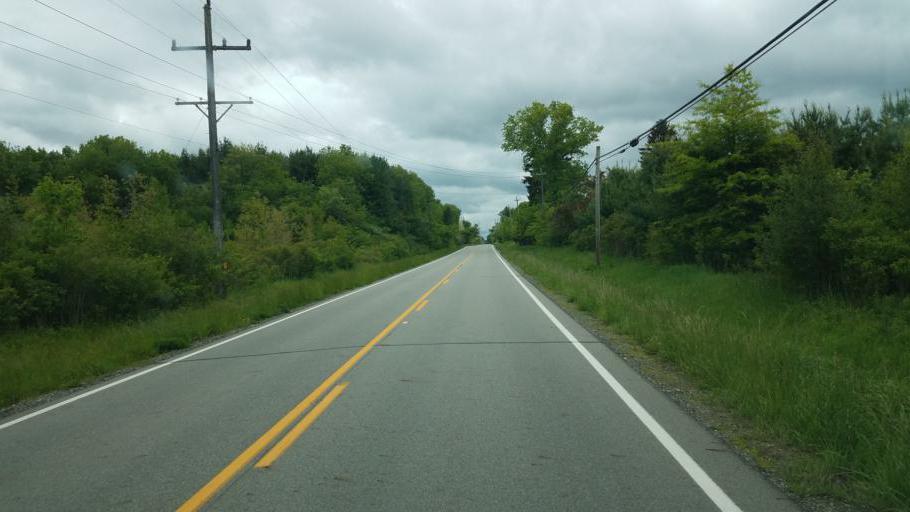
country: US
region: Ohio
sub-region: Geauga County
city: Burton
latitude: 41.4097
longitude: -81.1717
